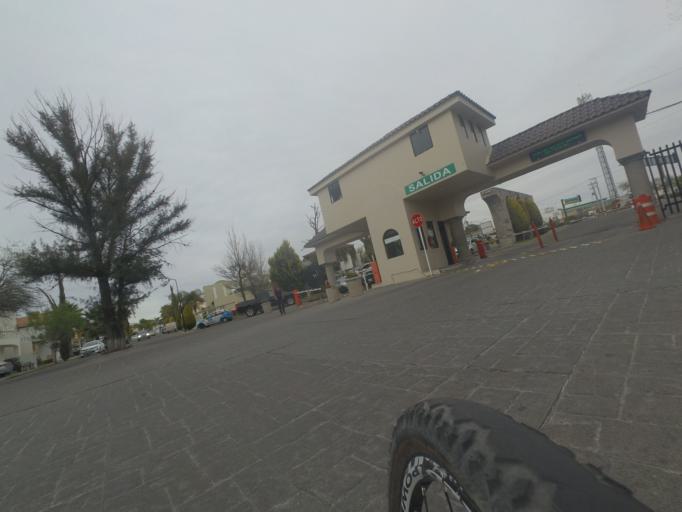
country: MX
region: Aguascalientes
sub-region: Aguascalientes
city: La Loma de los Negritos
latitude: 21.8508
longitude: -102.3542
